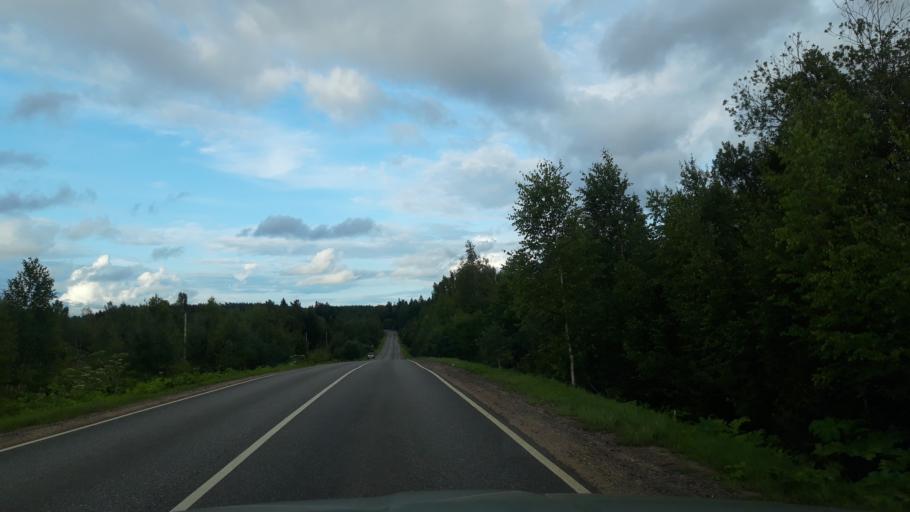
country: RU
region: Moskovskaya
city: Solnechnogorsk
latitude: 56.0937
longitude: 36.8335
